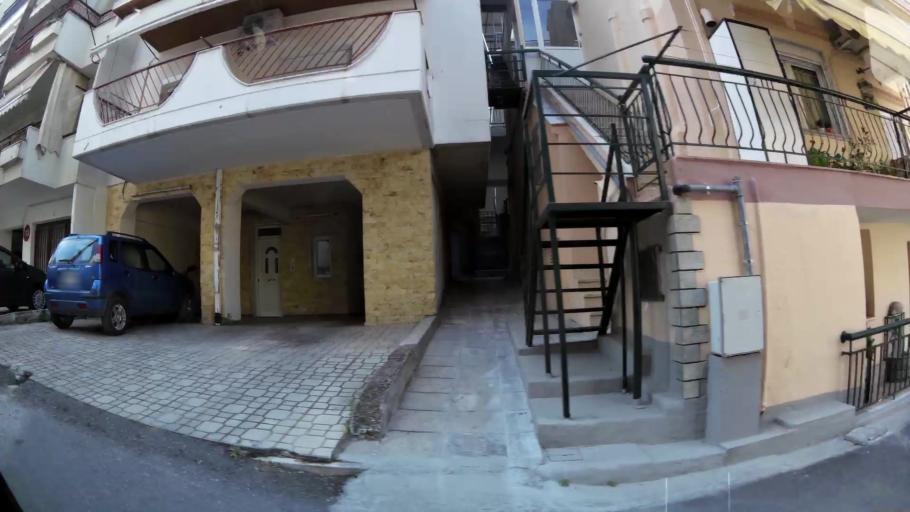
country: GR
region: Central Macedonia
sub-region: Nomos Thessalonikis
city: Sykies
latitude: 40.6532
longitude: 22.9517
